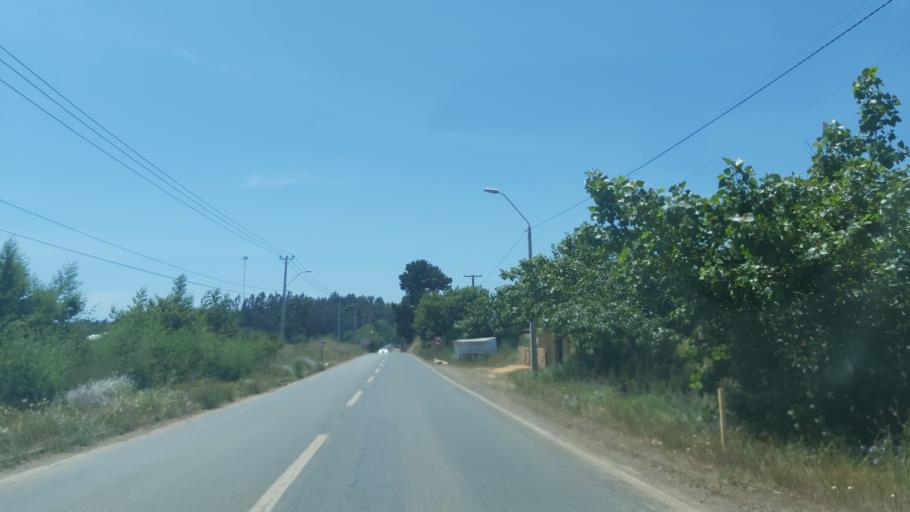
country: CL
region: Maule
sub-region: Provincia de Cauquenes
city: Cauquenes
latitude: -35.7948
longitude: -72.5465
